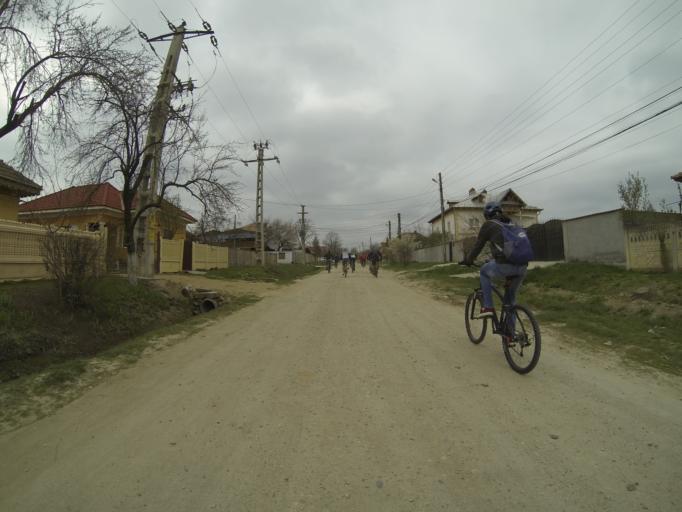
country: RO
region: Dolj
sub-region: Comuna Breasta
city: Breasta
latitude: 44.3404
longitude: 23.6865
